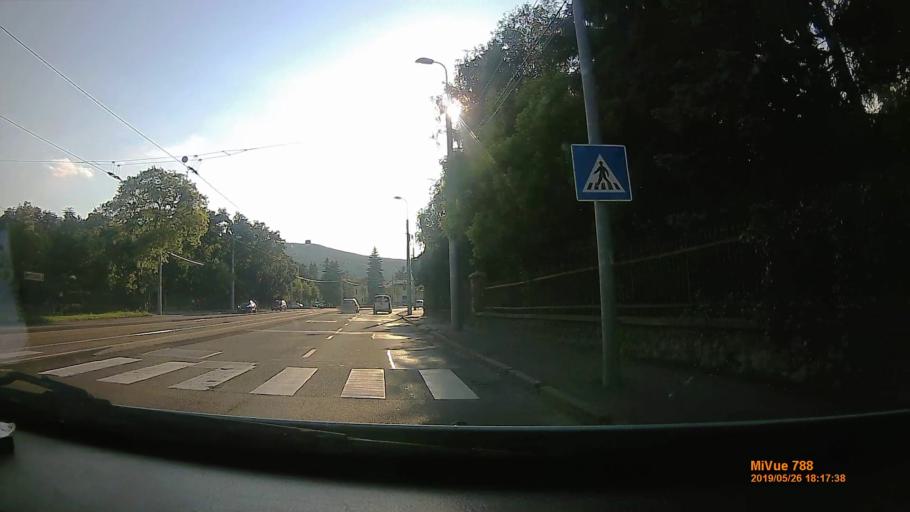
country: HU
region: Borsod-Abauj-Zemplen
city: Sajobabony
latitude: 48.0998
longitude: 20.6948
